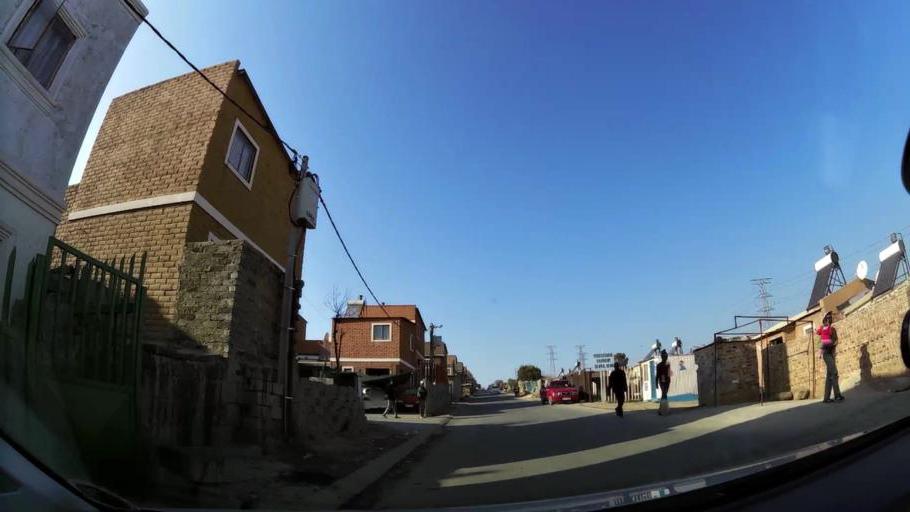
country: ZA
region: Gauteng
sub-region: City of Johannesburg Metropolitan Municipality
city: Modderfontein
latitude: -26.0945
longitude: 28.1083
